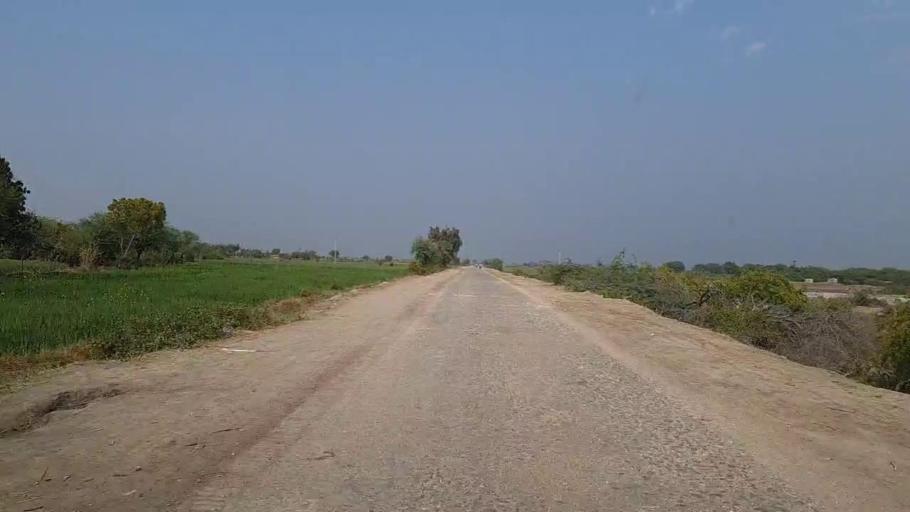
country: PK
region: Sindh
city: Mirwah Gorchani
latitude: 25.4105
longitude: 69.1424
